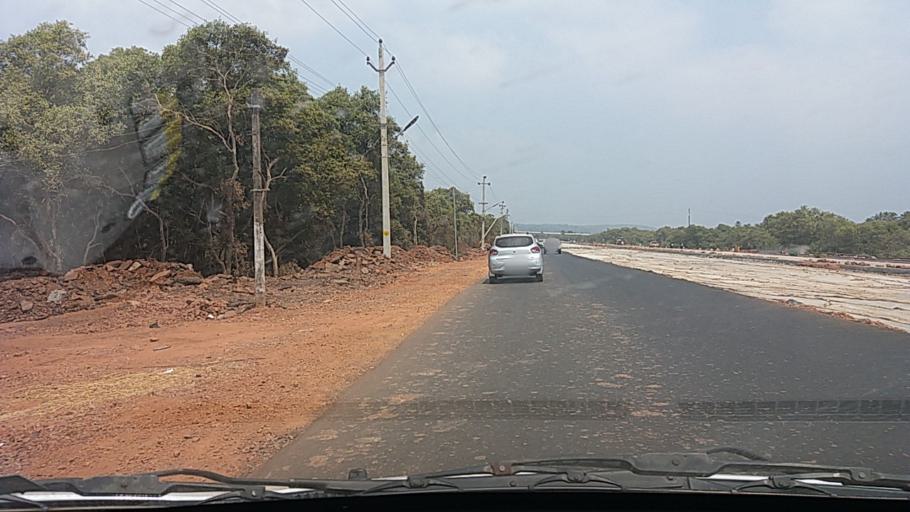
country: IN
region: Goa
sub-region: North Goa
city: Taleigao
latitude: 15.4839
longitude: 73.8469
